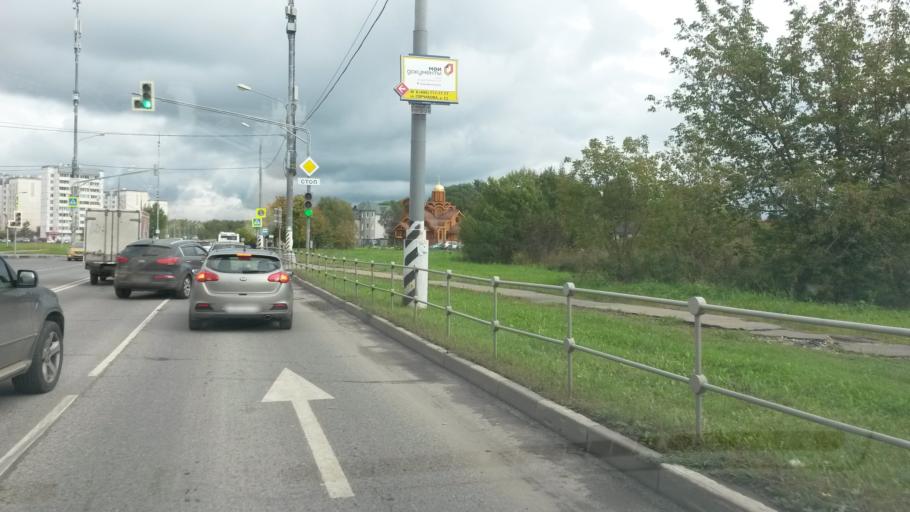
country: RU
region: Moskovskaya
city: Shcherbinka
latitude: 55.5339
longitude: 37.5365
